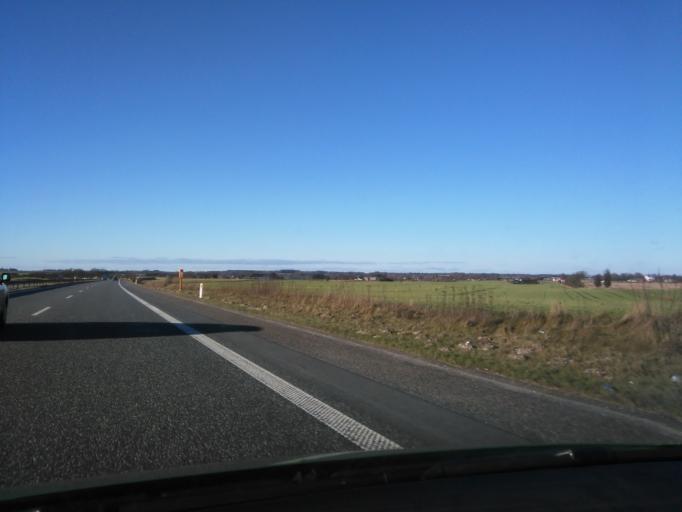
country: DK
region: Central Jutland
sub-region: Randers Kommune
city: Spentrup
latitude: 56.5317
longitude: 9.9298
